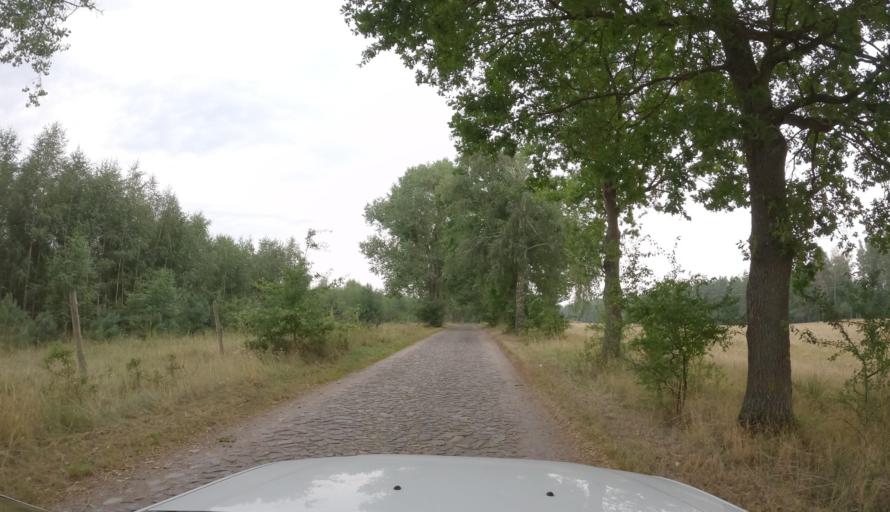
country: PL
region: West Pomeranian Voivodeship
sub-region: Powiat kolobrzeski
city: Ryman
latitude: 53.8521
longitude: 15.5869
